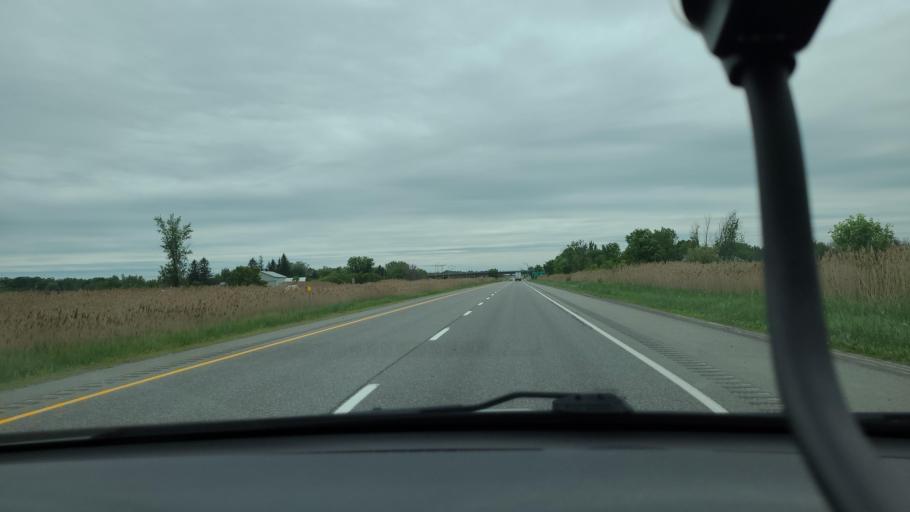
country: CA
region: Quebec
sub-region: Lanaudiere
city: Mascouche
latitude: 45.7574
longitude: -73.5832
